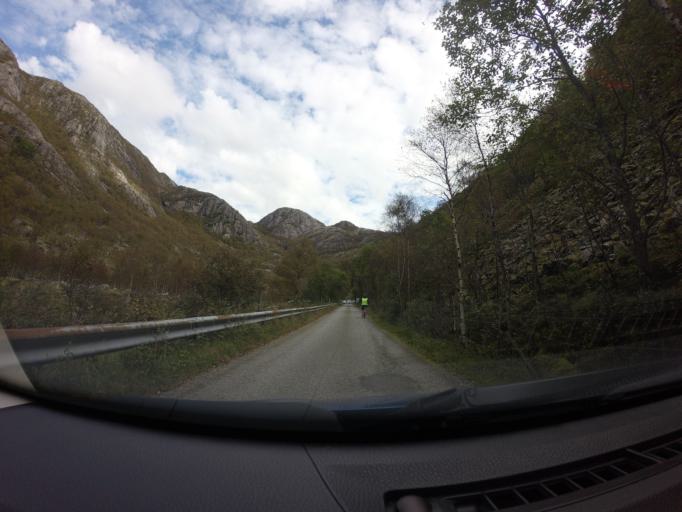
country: NO
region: Rogaland
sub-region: Forsand
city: Forsand
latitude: 58.8580
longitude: 6.3763
